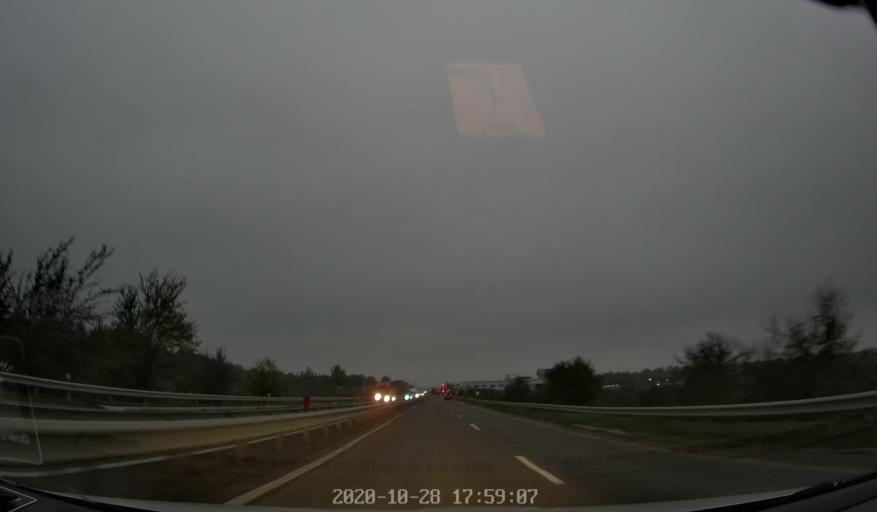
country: MD
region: Laloveni
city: Ialoveni
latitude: 46.9550
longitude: 28.7487
